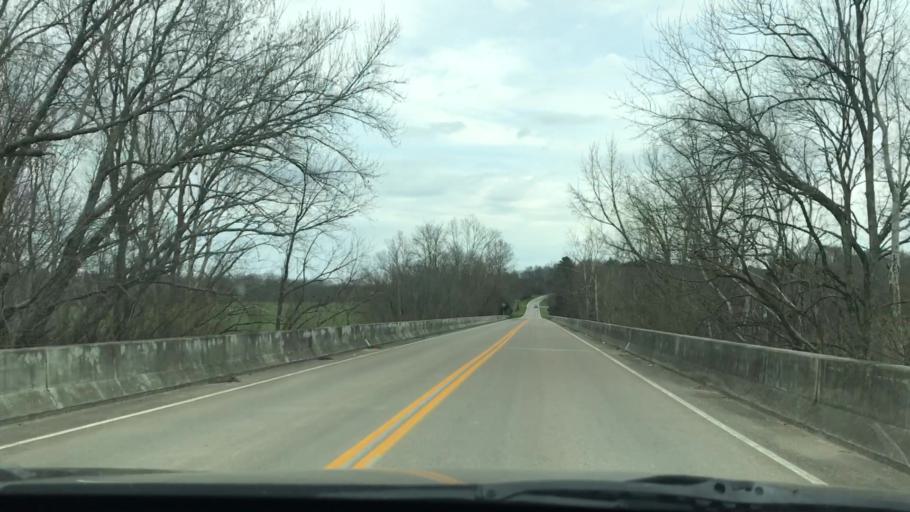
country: US
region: Kentucky
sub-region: Hart County
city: Munfordville
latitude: 37.3196
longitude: -85.7638
